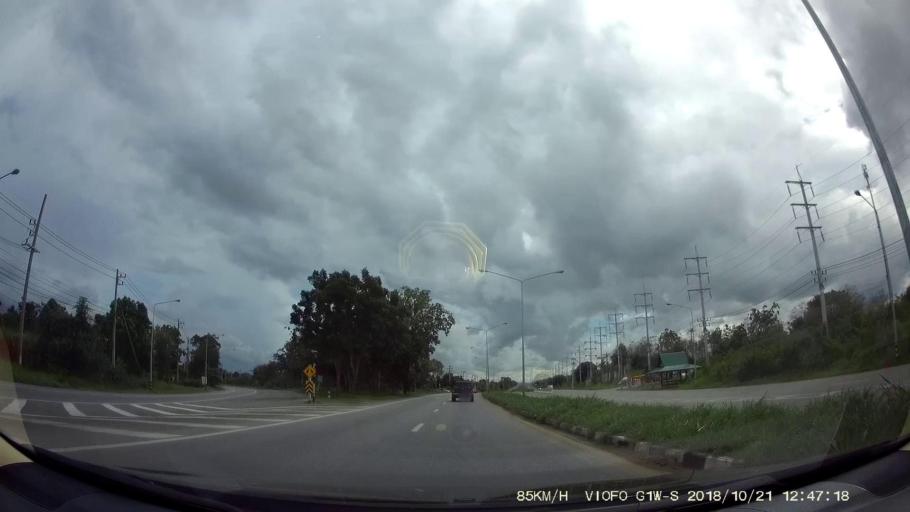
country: TH
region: Nakhon Ratchasima
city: Amphoe Sikhiu
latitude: 14.9302
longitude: 101.6838
